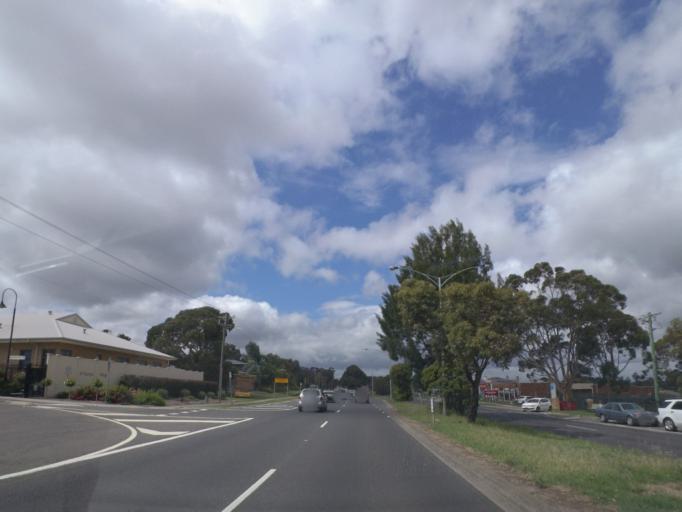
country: AU
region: Victoria
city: Plenty
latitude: -37.6810
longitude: 145.1216
